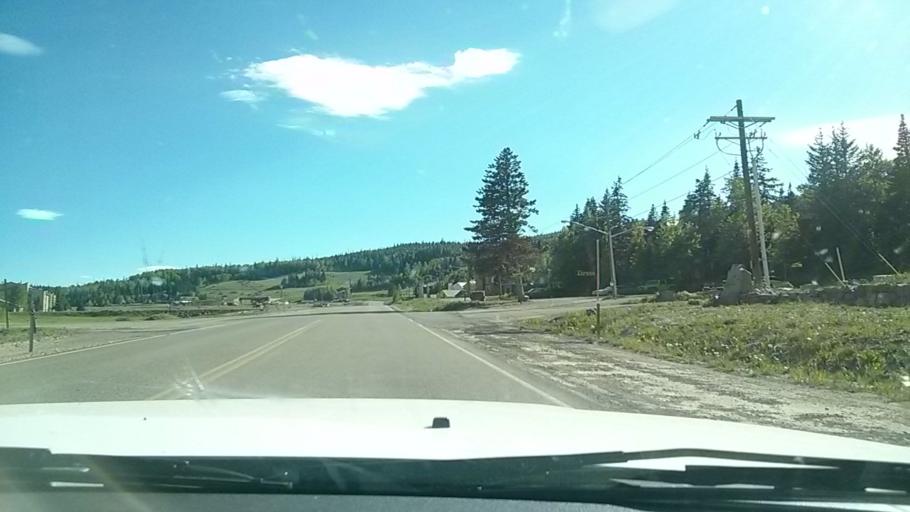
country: US
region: Utah
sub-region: Iron County
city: Parowan
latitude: 37.6935
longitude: -112.8489
